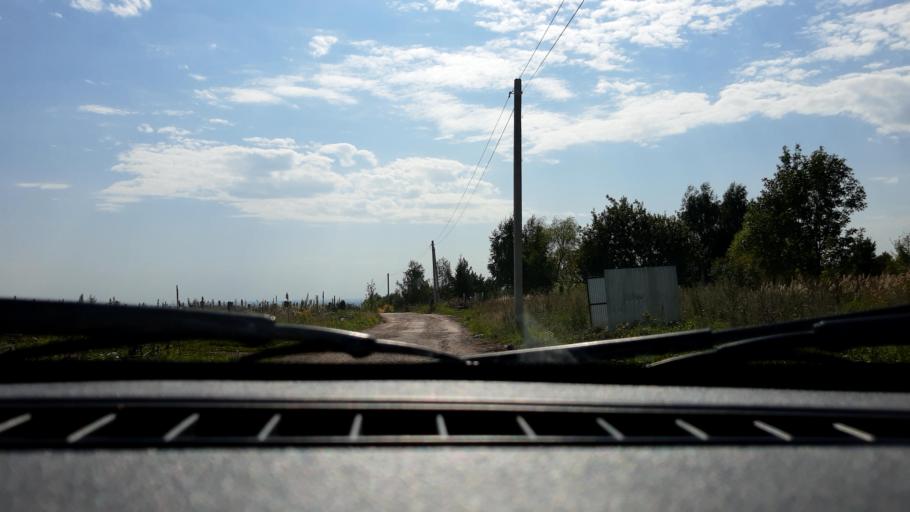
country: RU
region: Bashkortostan
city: Ufa
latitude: 54.8549
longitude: 56.1639
